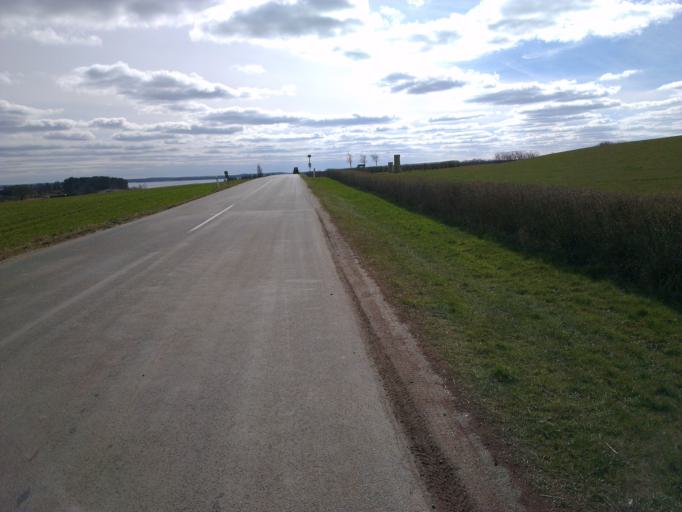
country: DK
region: Capital Region
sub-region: Frederikssund Kommune
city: Skibby
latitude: 55.7483
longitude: 11.9864
